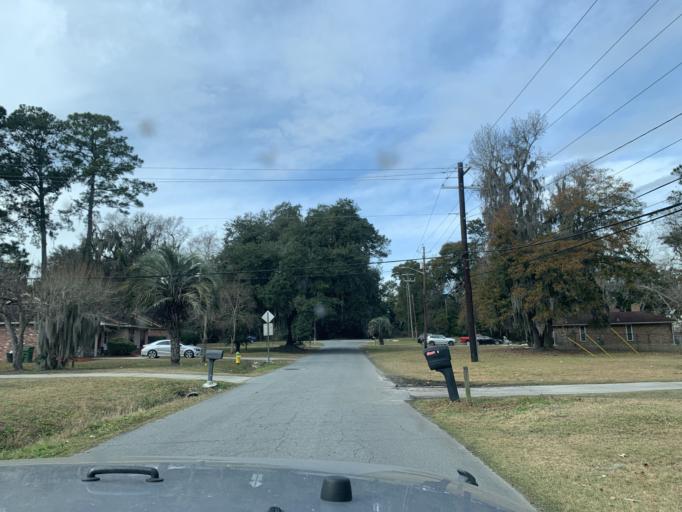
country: US
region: Georgia
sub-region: Chatham County
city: Montgomery
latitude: 31.9694
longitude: -81.1328
